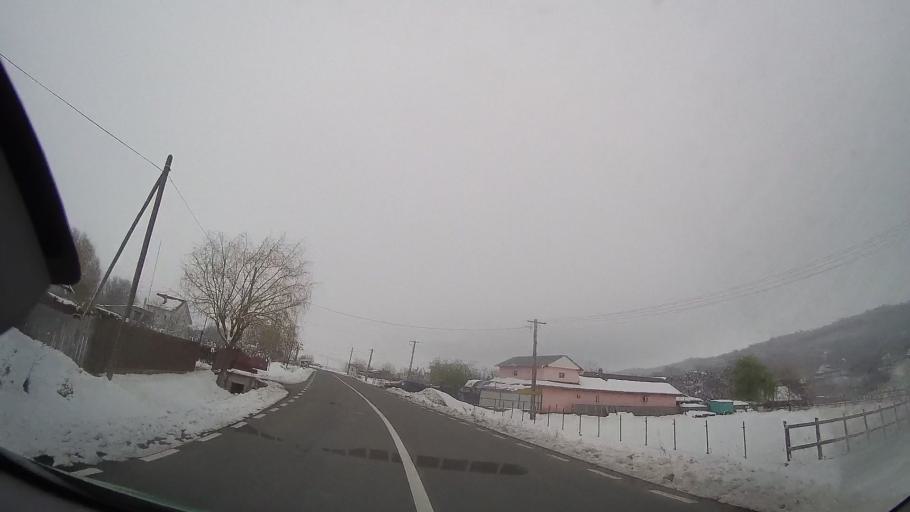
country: RO
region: Neamt
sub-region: Comuna Bozieni
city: Bozieni
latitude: 46.8531
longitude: 27.1777
